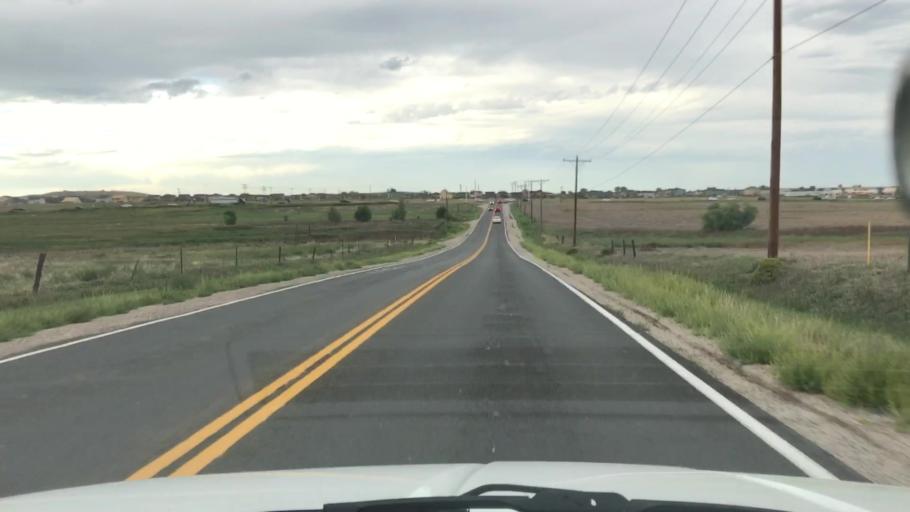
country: US
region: Colorado
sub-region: Boulder County
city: Erie
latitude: 39.9960
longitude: -104.9973
